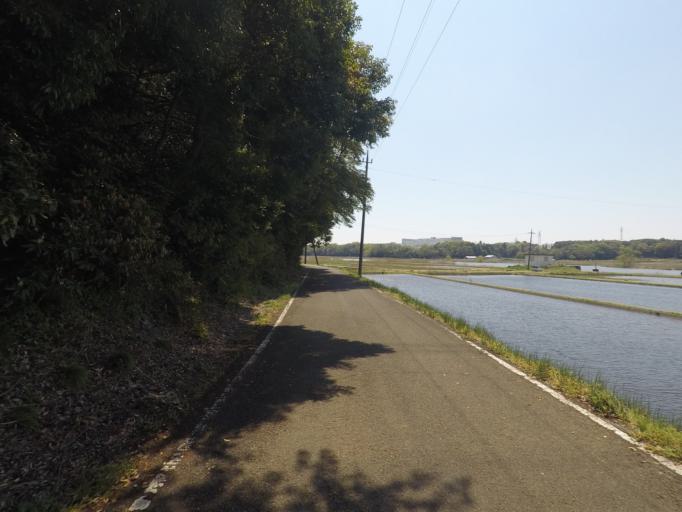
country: JP
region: Ibaraki
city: Ushiku
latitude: 36.0013
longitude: 140.0986
